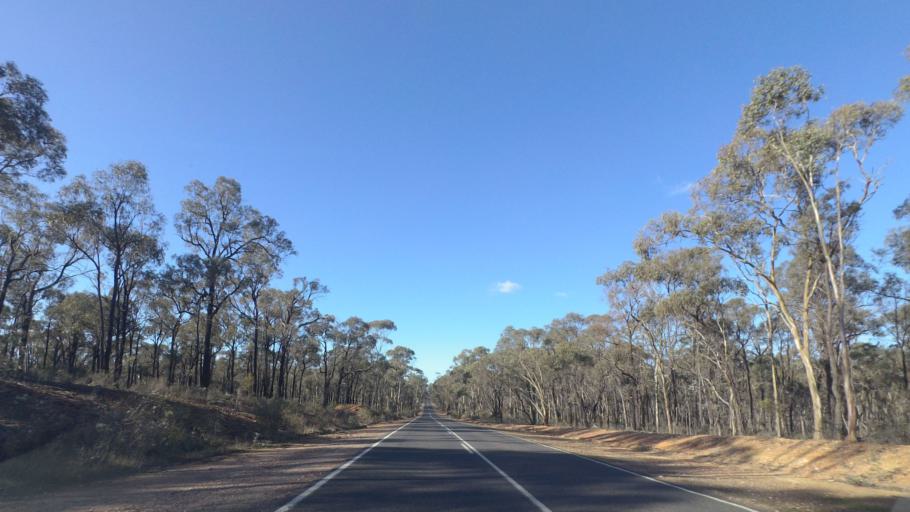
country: AU
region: Victoria
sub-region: Greater Bendigo
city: Epsom
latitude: -36.6665
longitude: 144.4349
